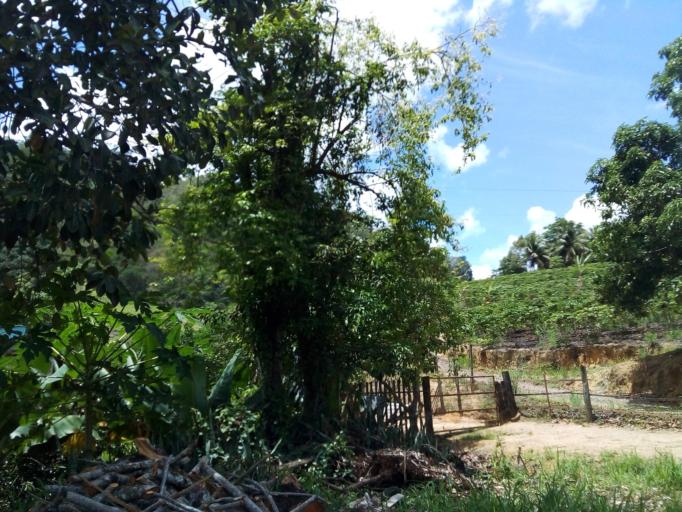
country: BR
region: Espirito Santo
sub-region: Fundao
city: Fundao
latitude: -19.9248
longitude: -40.3971
